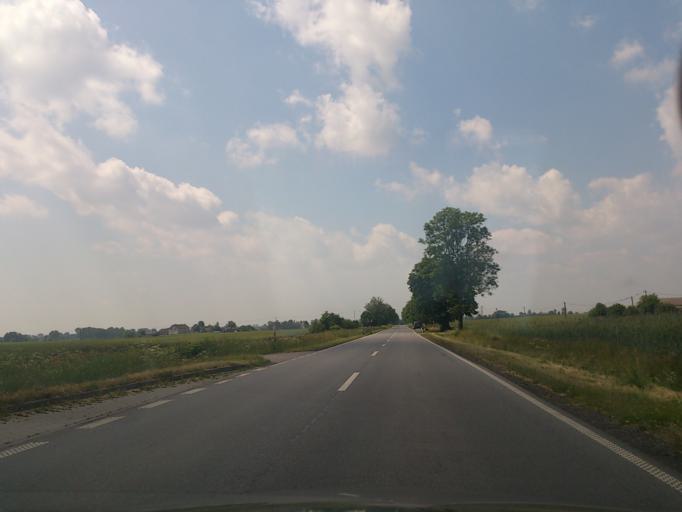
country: PL
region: Kujawsko-Pomorskie
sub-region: Powiat rypinski
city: Brzuze
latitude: 53.0686
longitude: 19.2688
